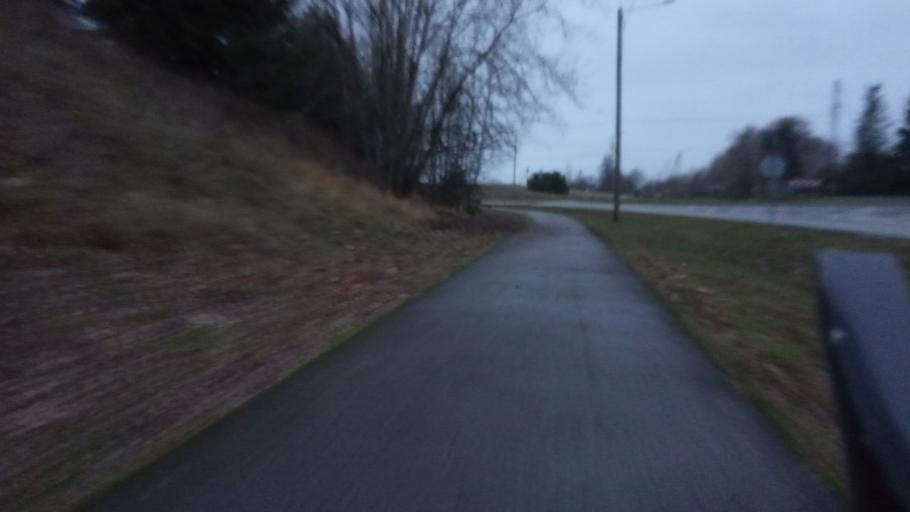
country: EE
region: Harju
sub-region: Kuusalu vald
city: Kuusalu
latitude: 59.4492
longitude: 25.4326
